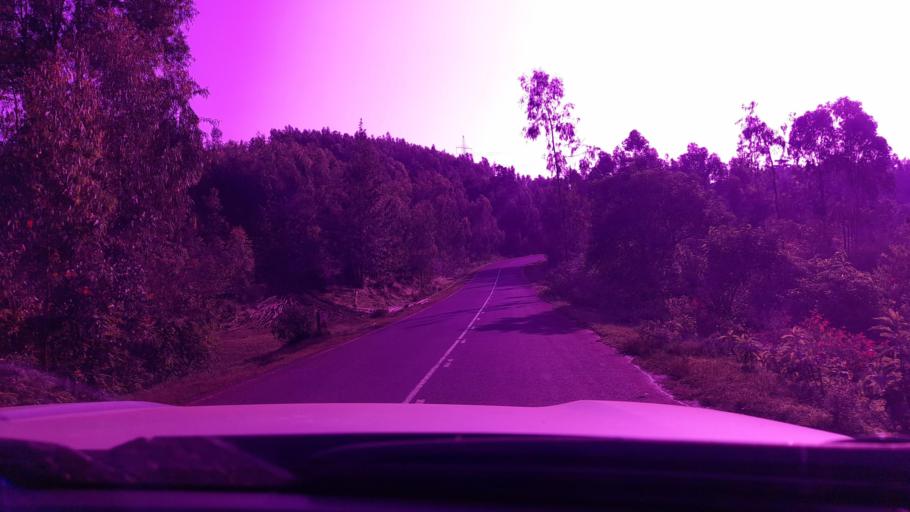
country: ET
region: Oromiya
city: Bedele
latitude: 8.1391
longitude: 36.4522
